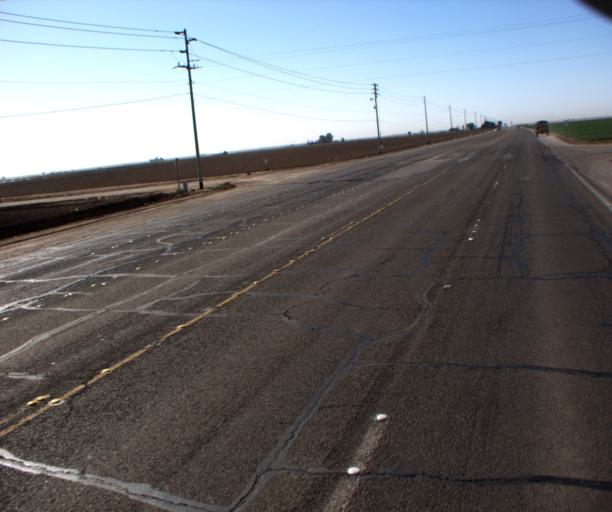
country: US
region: Arizona
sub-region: Yuma County
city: Somerton
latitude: 32.5824
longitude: -114.7699
